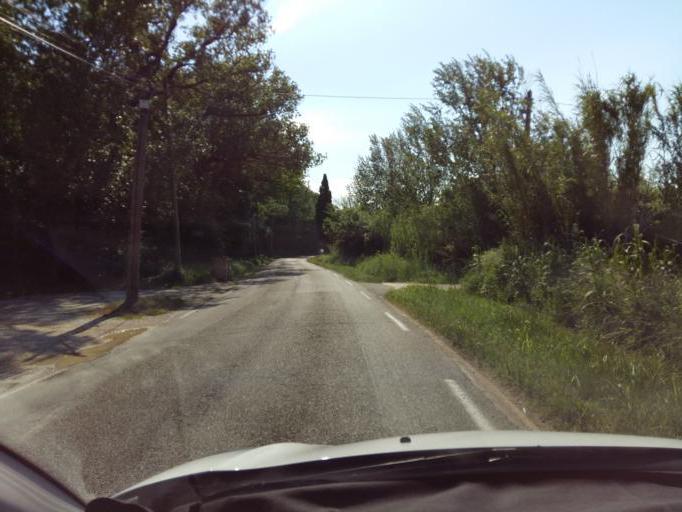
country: FR
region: Provence-Alpes-Cote d'Azur
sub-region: Departement du Vaucluse
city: Taillades
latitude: 43.8504
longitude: 5.0637
